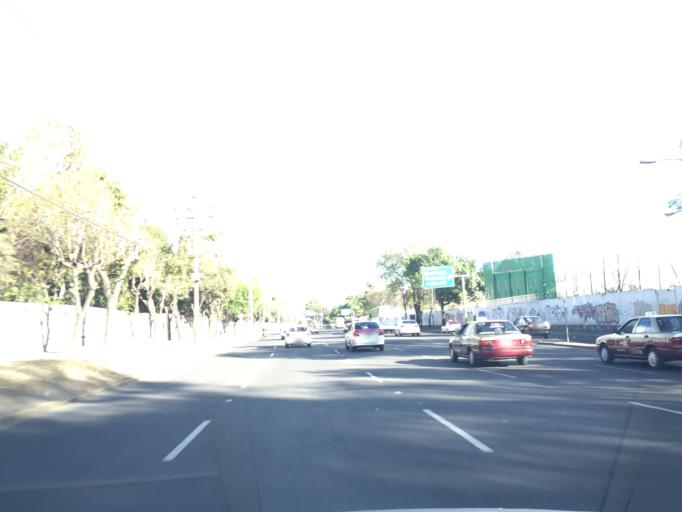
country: MX
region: Mexico
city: Colonia Lindavista
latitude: 19.4862
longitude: -99.1417
